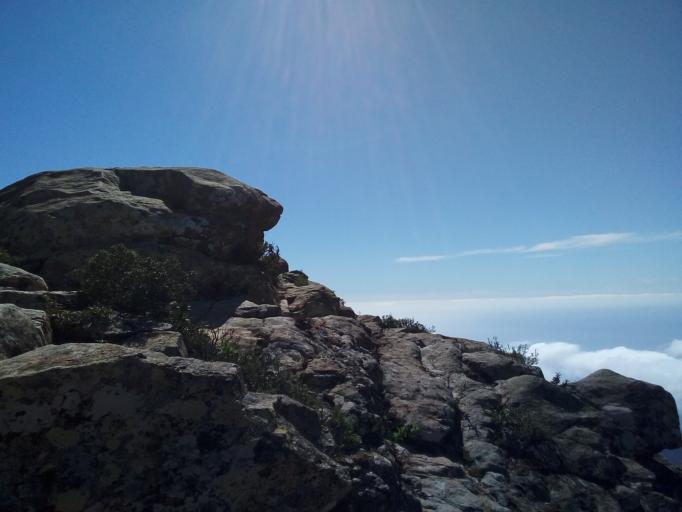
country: ES
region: Canary Islands
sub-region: Provincia de Santa Cruz de Tenerife
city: Alajero
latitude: 28.0982
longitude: -17.2771
